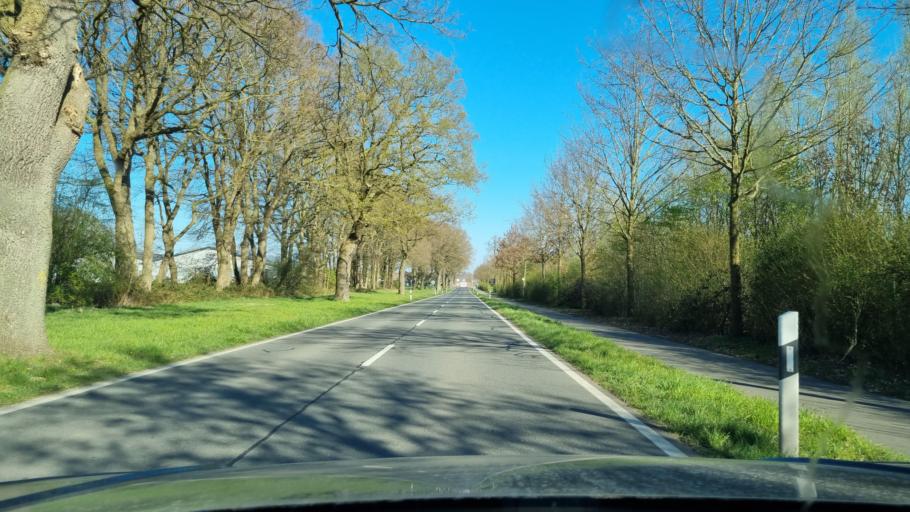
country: DE
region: North Rhine-Westphalia
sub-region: Regierungsbezirk Dusseldorf
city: Goch
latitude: 51.7025
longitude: 6.1147
